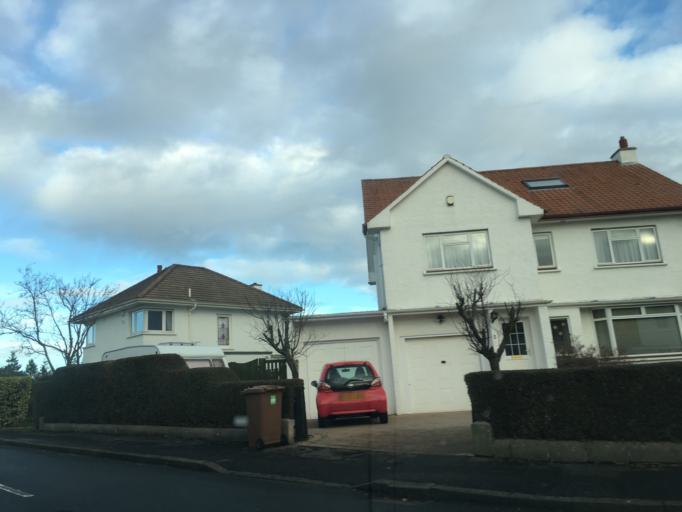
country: GB
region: Scotland
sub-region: Edinburgh
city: Colinton
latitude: 55.9020
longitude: -3.2572
